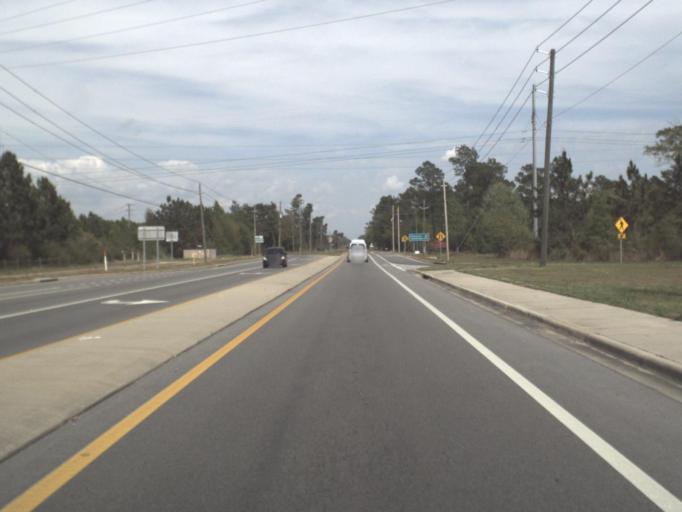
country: US
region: Florida
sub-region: Santa Rosa County
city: East Milton
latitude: 30.6352
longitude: -86.9710
